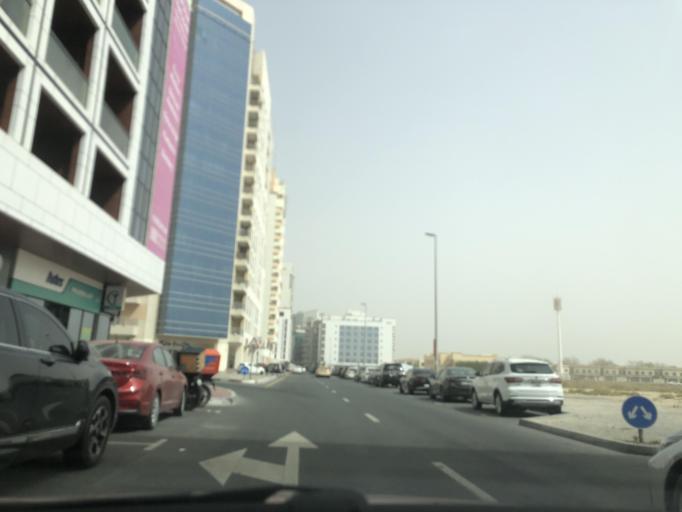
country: AE
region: Dubai
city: Dubai
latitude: 25.1108
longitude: 55.1953
